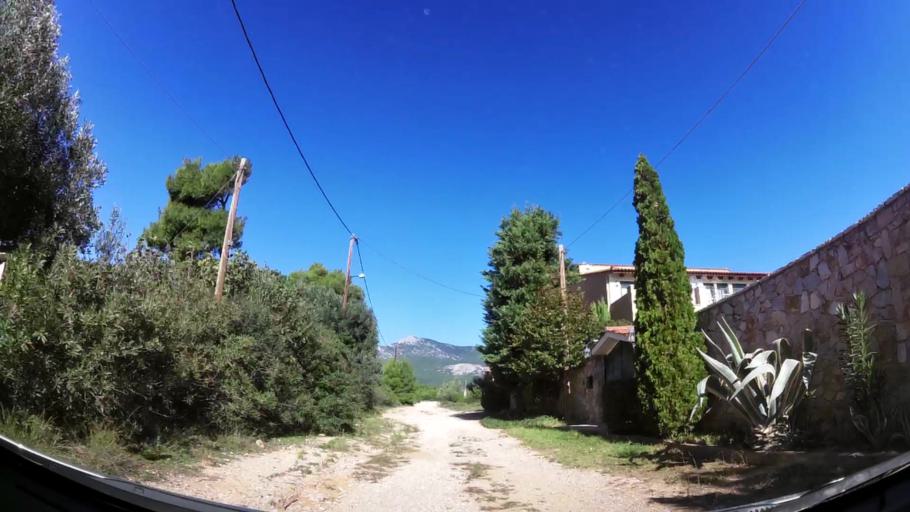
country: GR
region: Attica
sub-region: Nomarchia Anatolikis Attikis
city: Varybobi
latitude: 38.1208
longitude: 23.7808
